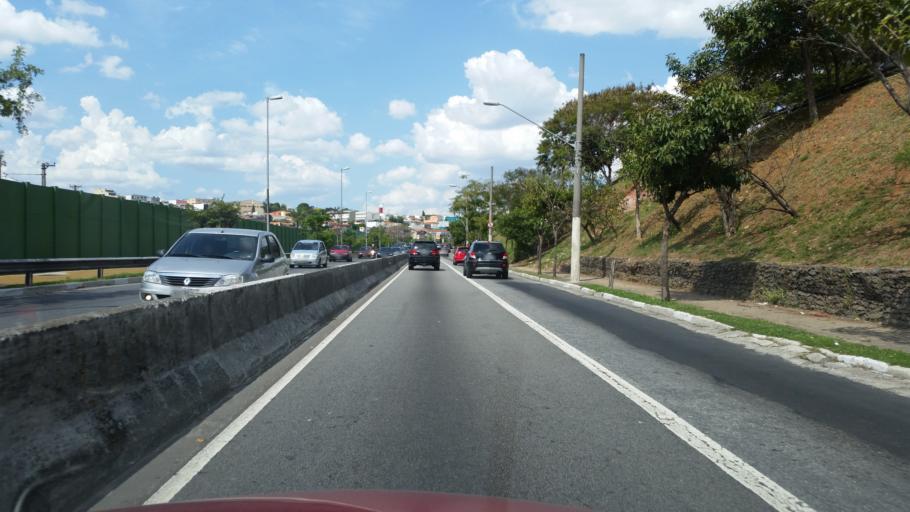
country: BR
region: Sao Paulo
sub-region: Guarulhos
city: Guarulhos
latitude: -23.5281
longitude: -46.5121
